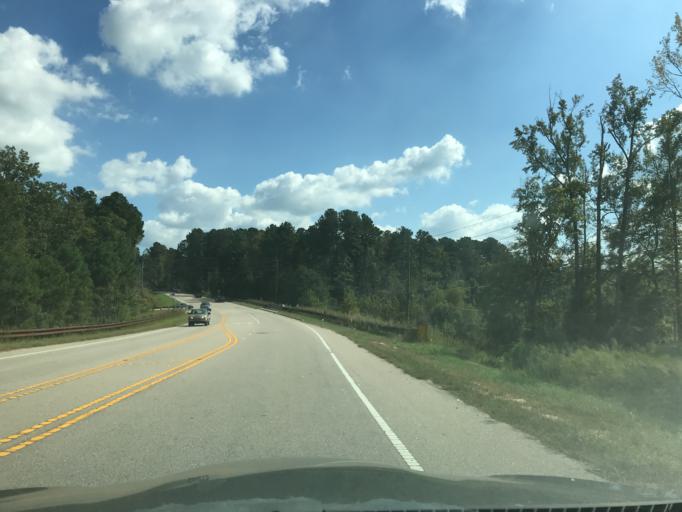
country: US
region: North Carolina
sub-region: Wake County
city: Rolesville
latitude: 35.9099
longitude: -78.5278
